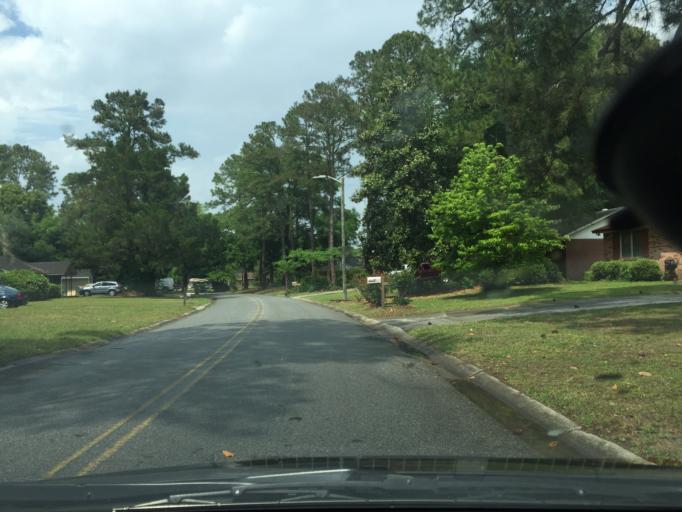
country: US
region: Georgia
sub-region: Chatham County
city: Montgomery
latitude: 31.9901
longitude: -81.1224
